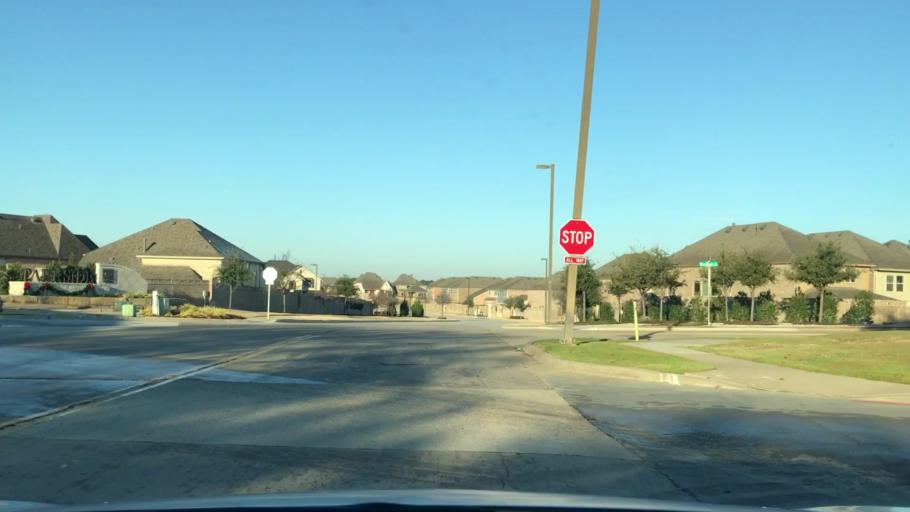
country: US
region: Texas
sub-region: Dallas County
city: Coppell
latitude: 32.8988
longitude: -96.9831
